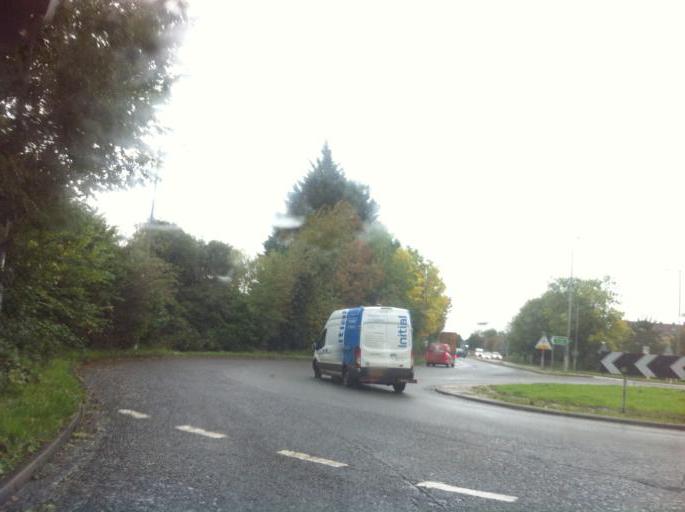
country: GB
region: England
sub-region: Lincolnshire
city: Boston
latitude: 52.9629
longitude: -0.0272
